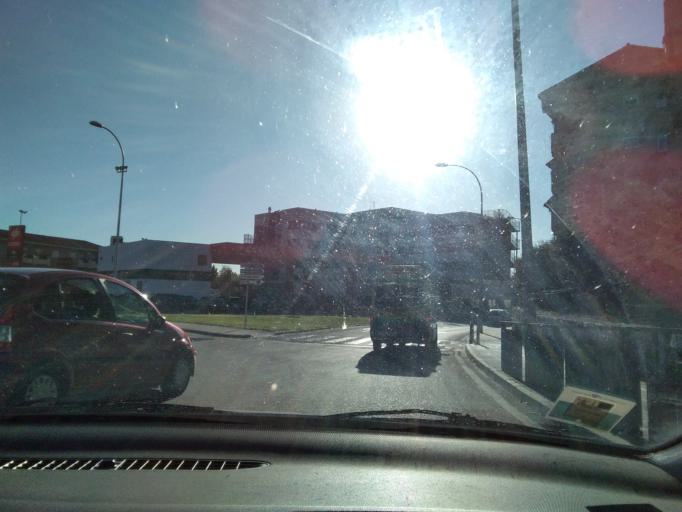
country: ES
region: Castille-La Mancha
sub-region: Province of Toledo
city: Toledo
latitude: 39.8727
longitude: -4.0394
